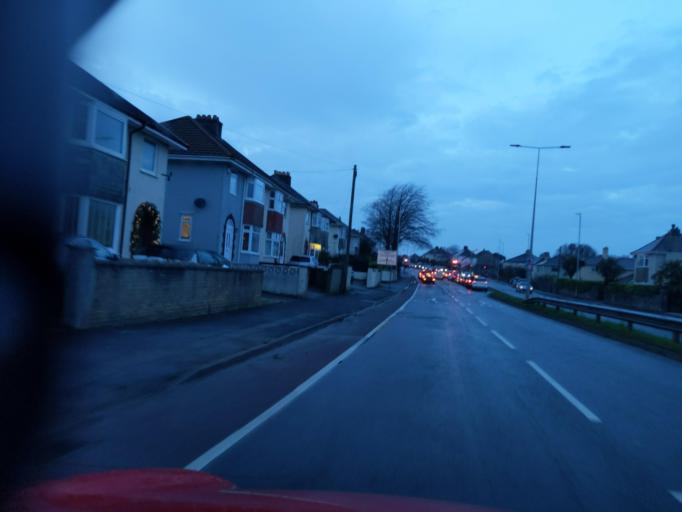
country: GB
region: England
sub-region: Plymouth
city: Plymstock
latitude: 50.3604
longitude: -4.0645
